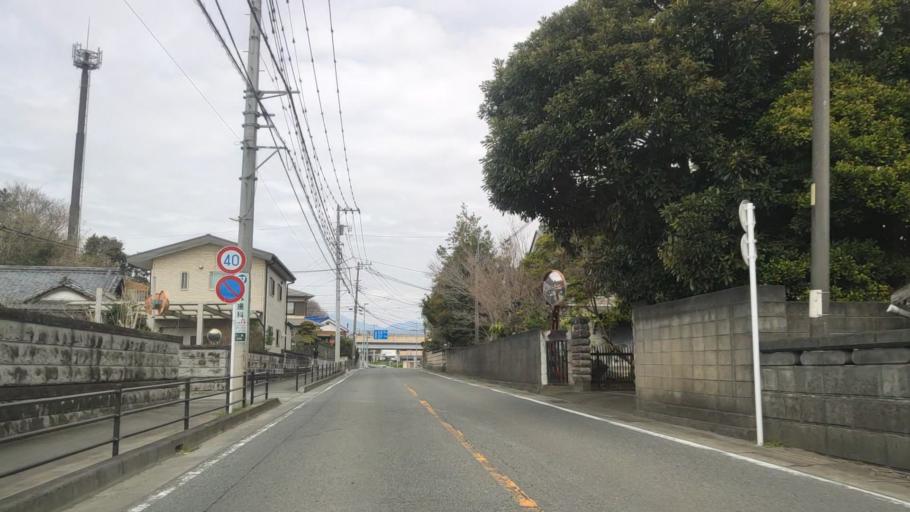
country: JP
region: Kanagawa
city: Ninomiya
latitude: 35.3041
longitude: 139.2267
